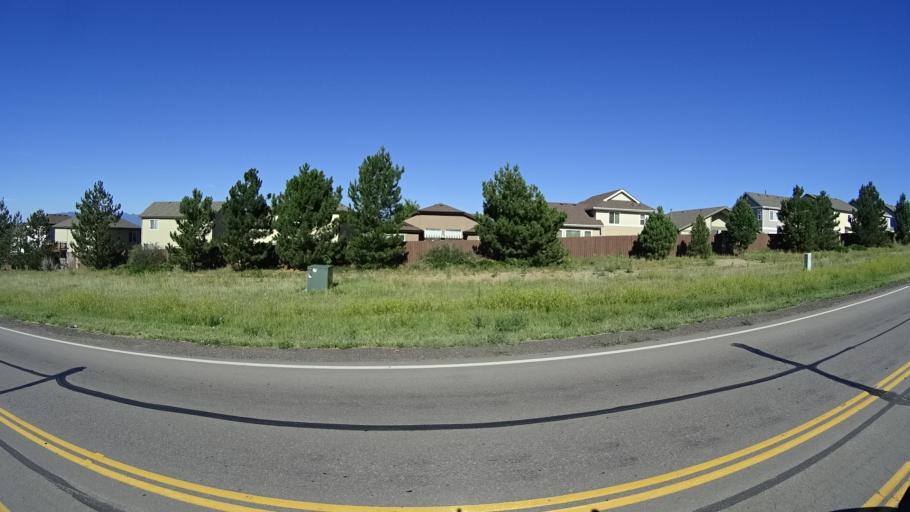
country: US
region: Colorado
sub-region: El Paso County
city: Cimarron Hills
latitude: 38.9079
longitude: -104.6829
